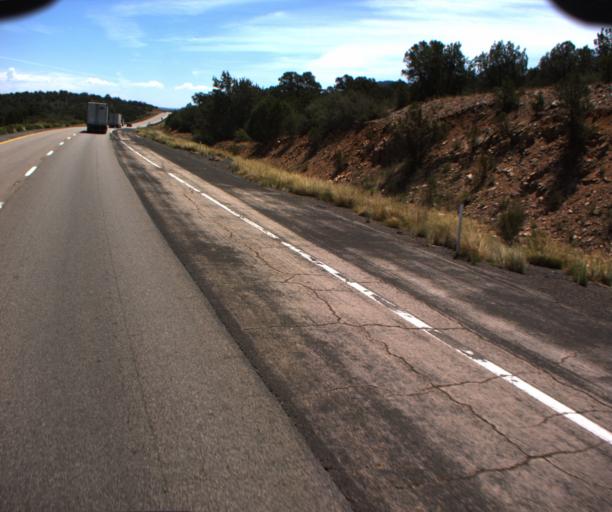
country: US
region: Arizona
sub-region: Mohave County
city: Peach Springs
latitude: 35.2074
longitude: -113.2895
